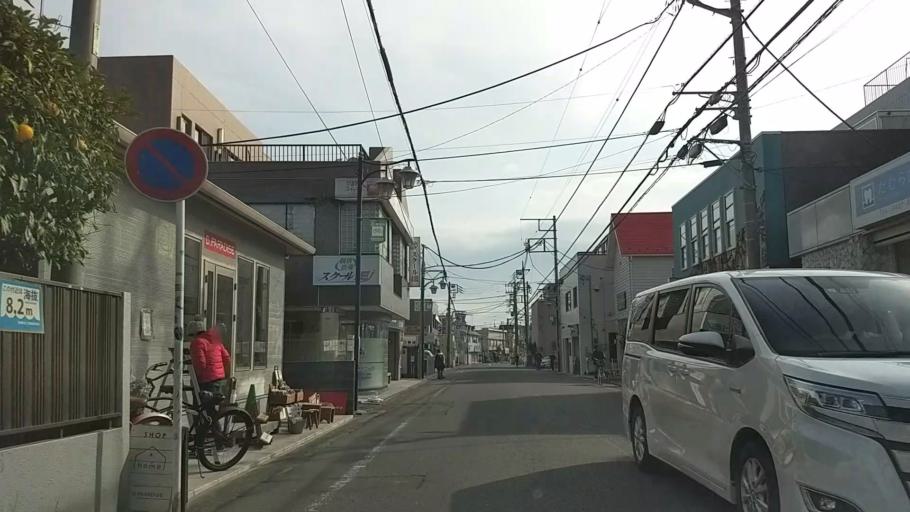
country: JP
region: Kanagawa
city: Chigasaki
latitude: 35.3274
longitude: 139.4079
